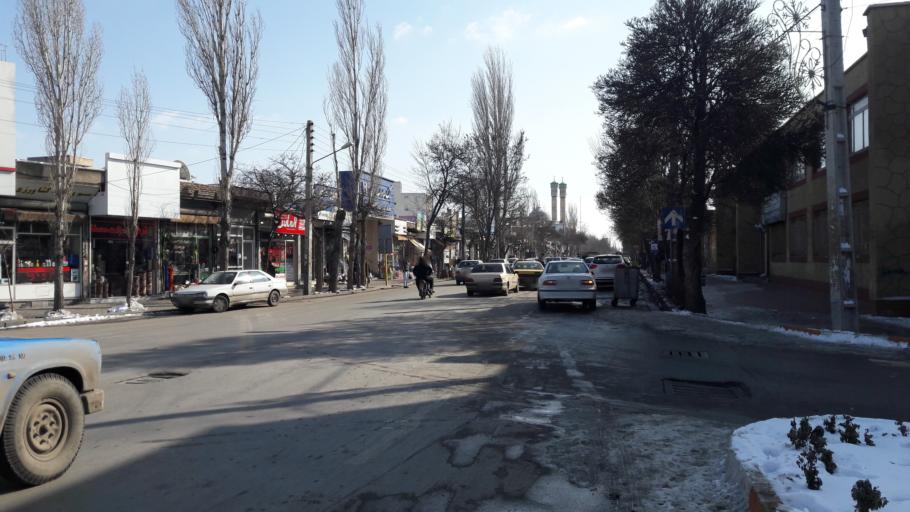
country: IR
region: Ardabil
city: Ardabil
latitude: 38.2560
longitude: 48.2939
